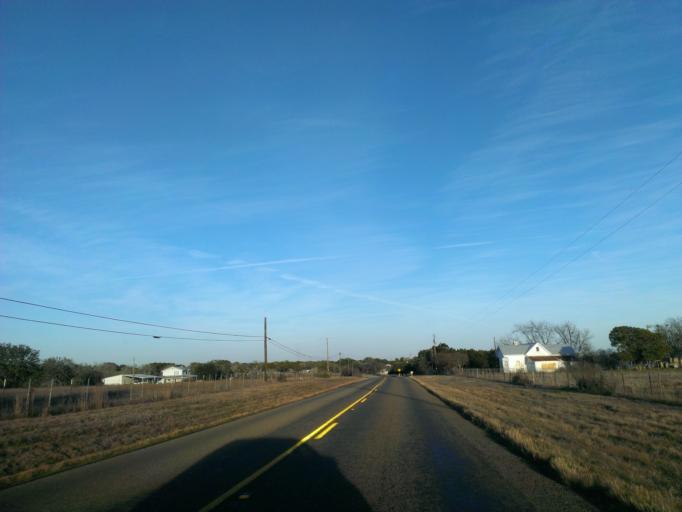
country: US
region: Texas
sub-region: Burnet County
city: Bertram
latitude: 30.7268
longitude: -98.0894
